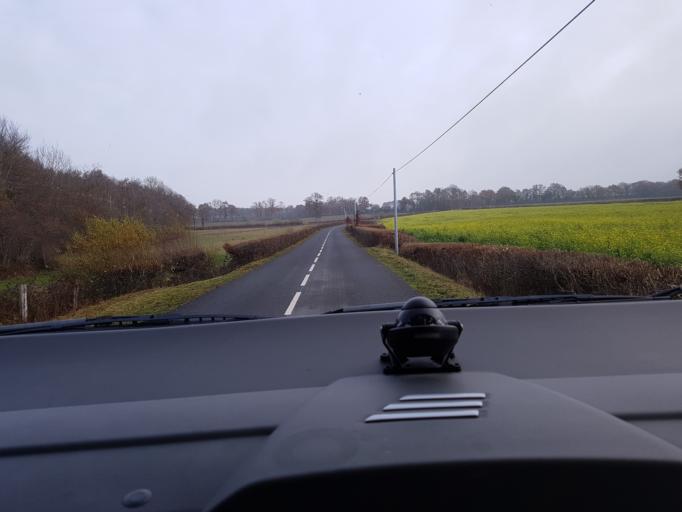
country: FR
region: Lower Normandy
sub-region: Departement de l'Orne
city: Mortree
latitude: 48.6312
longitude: -0.0319
